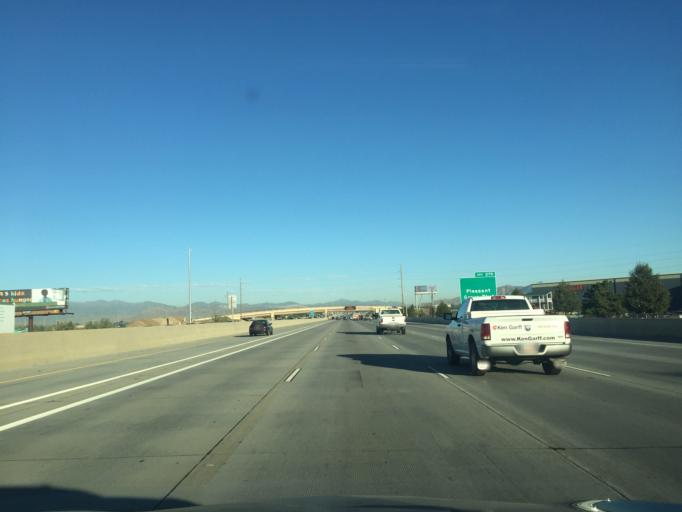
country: US
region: Utah
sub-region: Utah County
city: Pleasant Grove
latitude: 40.3421
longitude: -111.7564
